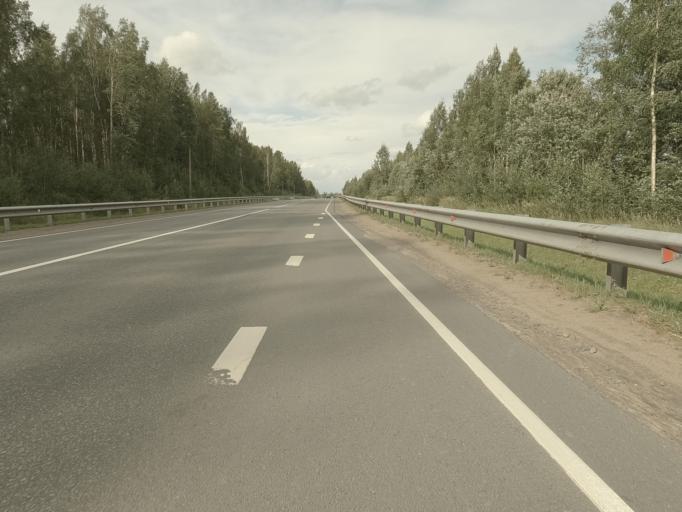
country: RU
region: Leningrad
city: Mga
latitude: 59.7870
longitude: 31.1067
